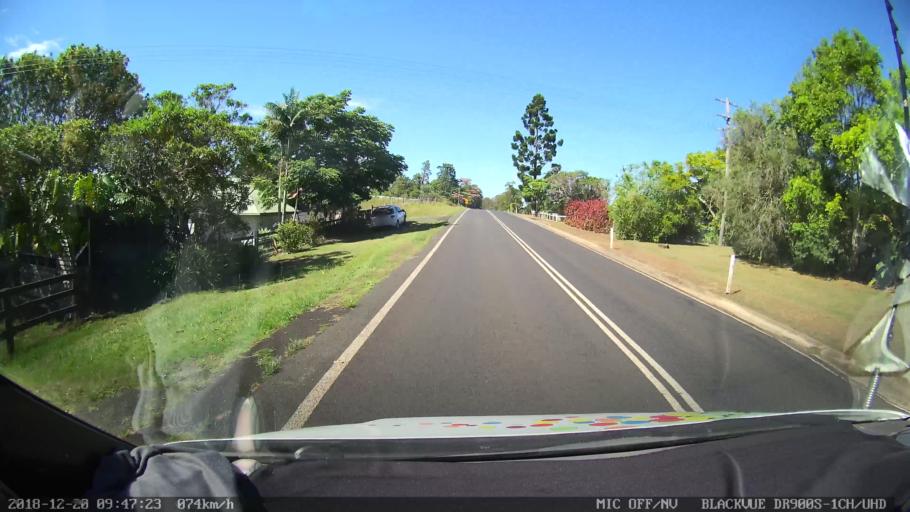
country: AU
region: New South Wales
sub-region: Lismore Municipality
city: Lismore
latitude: -28.7625
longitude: 153.2977
